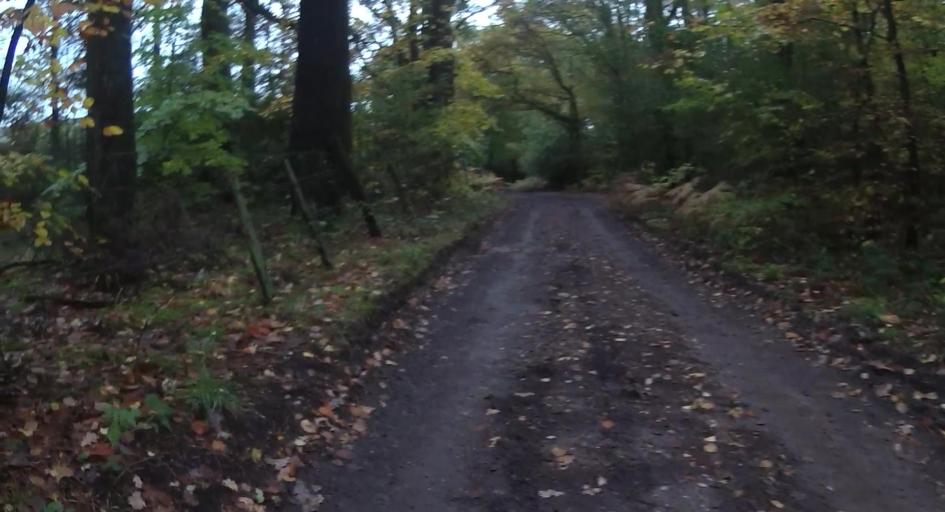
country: GB
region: England
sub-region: Surrey
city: Farnham
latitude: 51.2316
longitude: -0.8135
